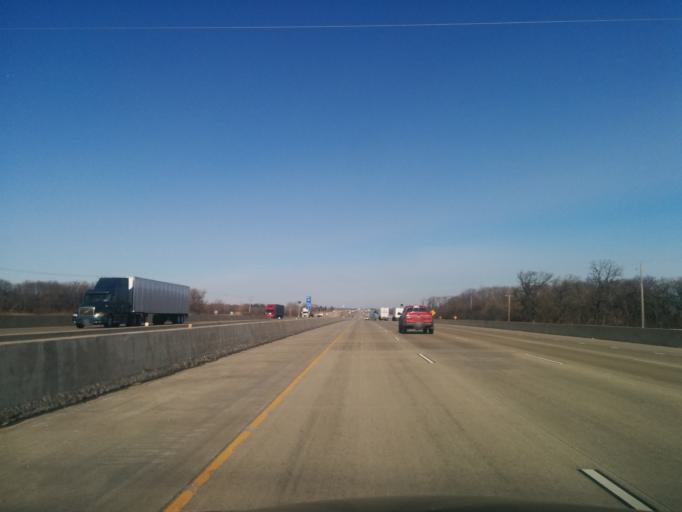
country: US
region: Wisconsin
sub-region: Kenosha County
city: Pleasant Prairie
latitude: 42.5053
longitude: -87.9515
